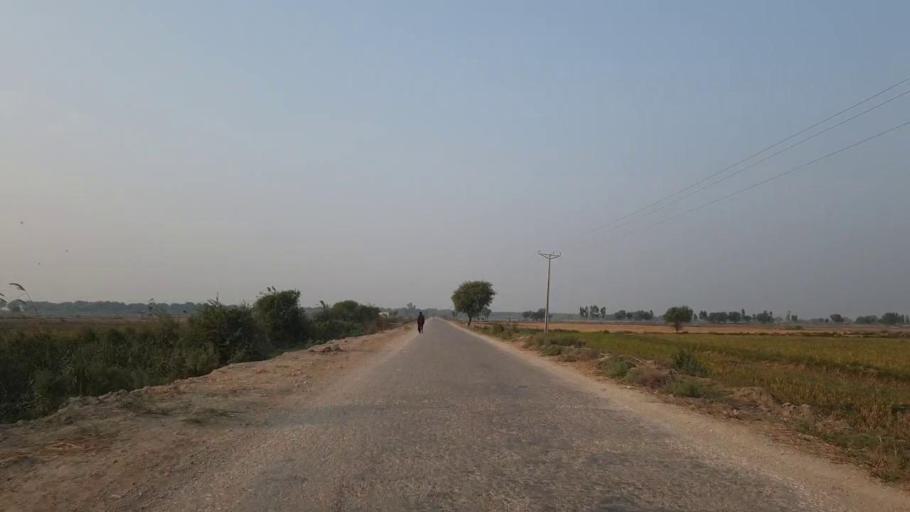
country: PK
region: Sindh
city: Tando Muhammad Khan
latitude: 25.1068
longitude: 68.4301
